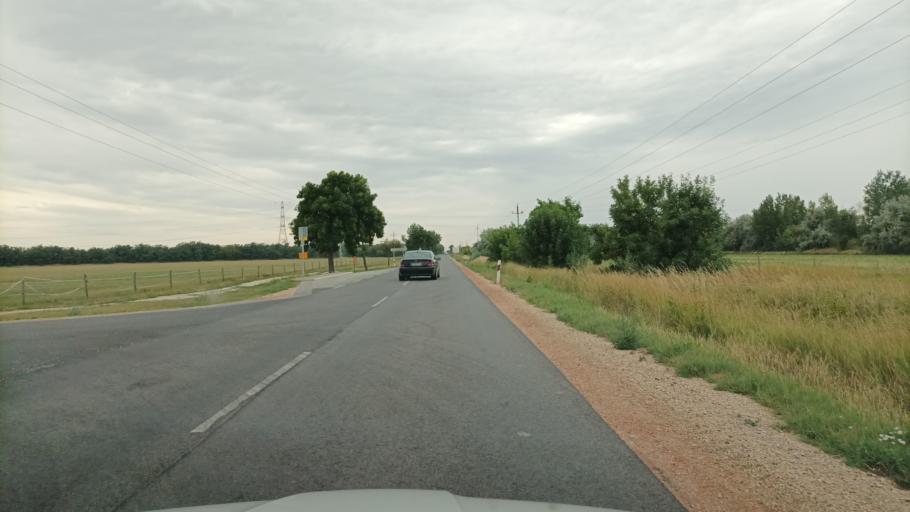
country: HU
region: Pest
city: Bugyi
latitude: 47.2360
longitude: 19.1864
